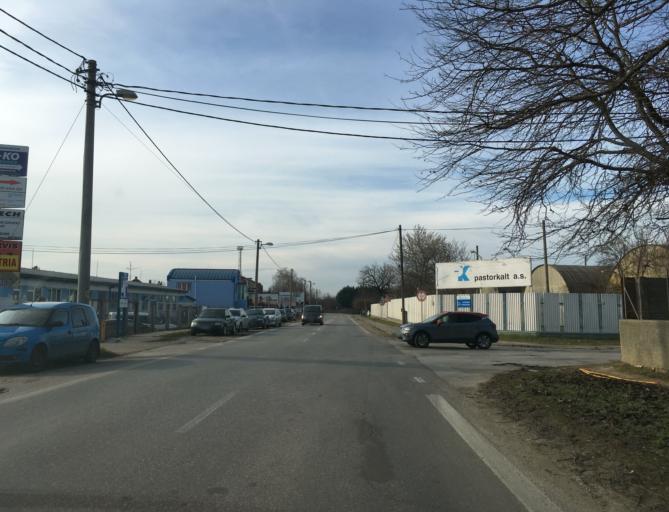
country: SK
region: Nitriansky
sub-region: Okres Nove Zamky
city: Nove Zamky
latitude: 48.0033
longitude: 18.1651
